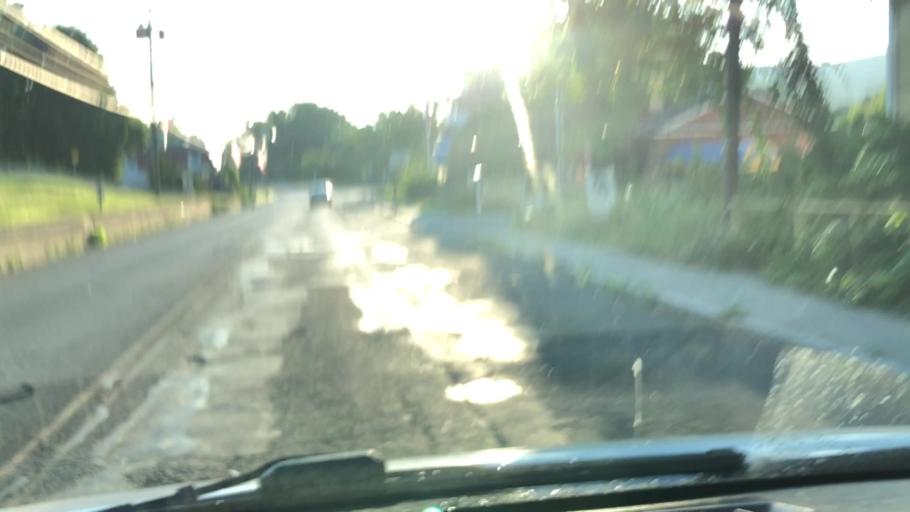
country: US
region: Massachusetts
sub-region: Hampshire County
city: Easthampton
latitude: 42.2756
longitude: -72.6586
